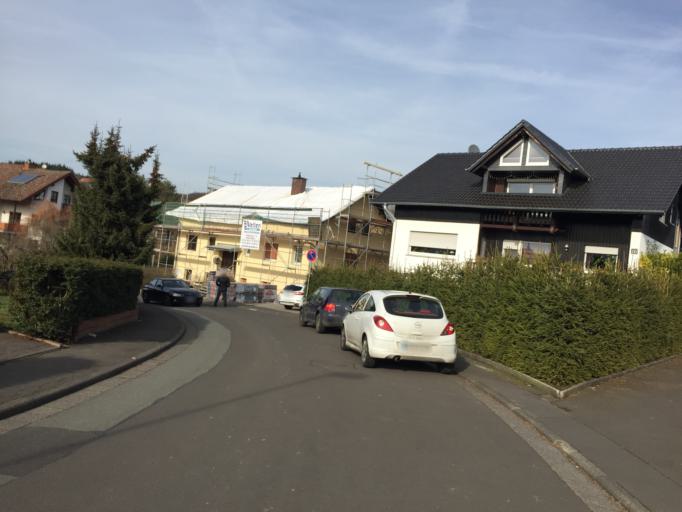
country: DE
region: Hesse
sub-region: Regierungsbezirk Giessen
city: Fronhausen
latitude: 50.6851
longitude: 8.6871
